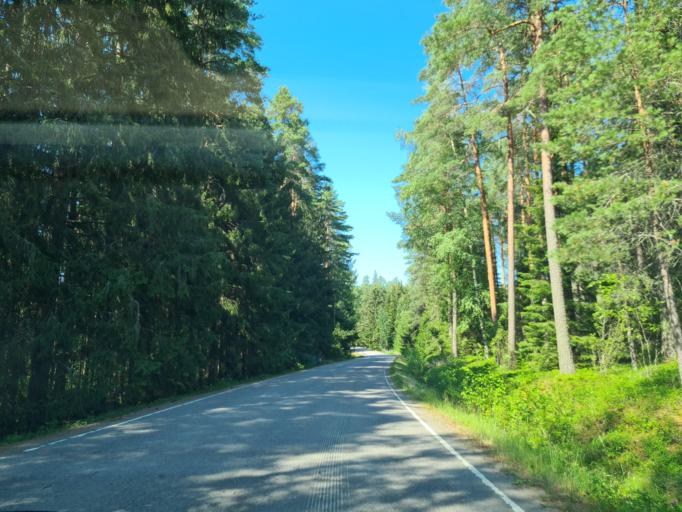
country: FI
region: Varsinais-Suomi
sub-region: Turku
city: Tarvasjoki
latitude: 60.5967
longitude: 22.6596
